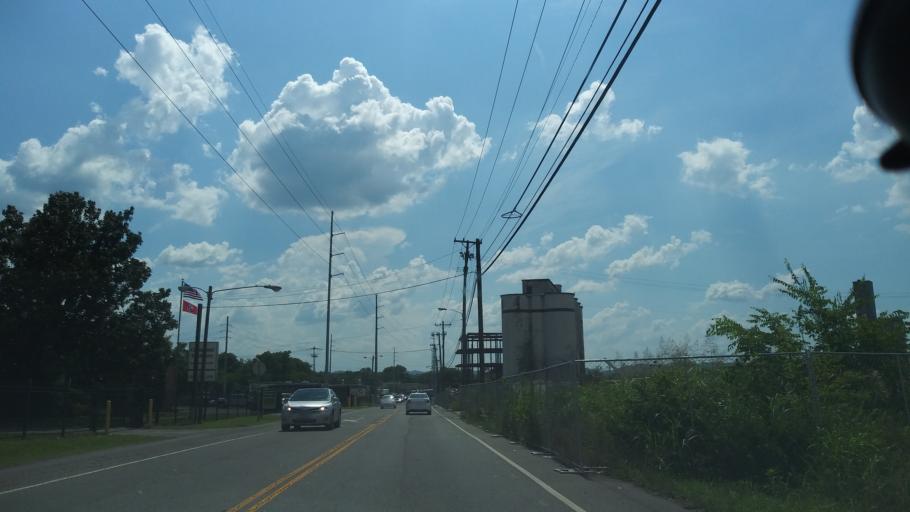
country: US
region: Tennessee
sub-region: Davidson County
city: Nashville
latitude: 36.1631
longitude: -86.8445
